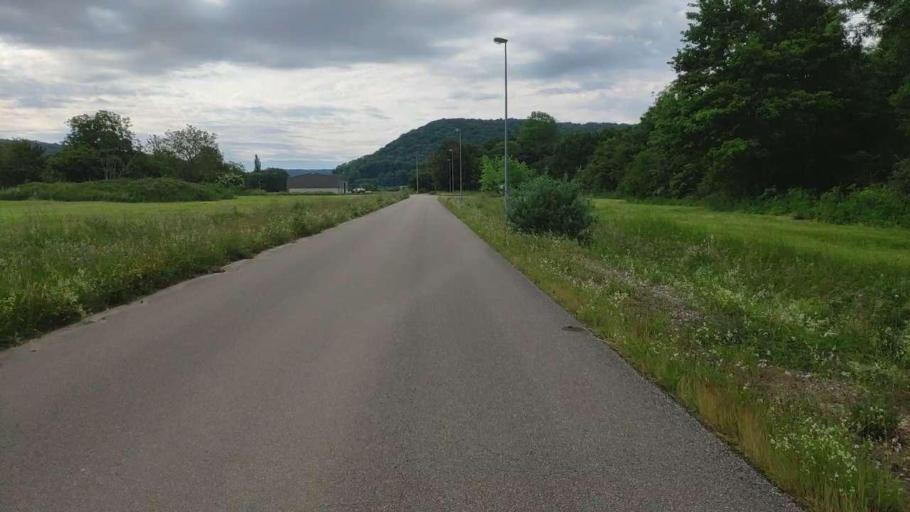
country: FR
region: Franche-Comte
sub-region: Departement du Jura
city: Perrigny
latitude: 46.7565
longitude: 5.6005
